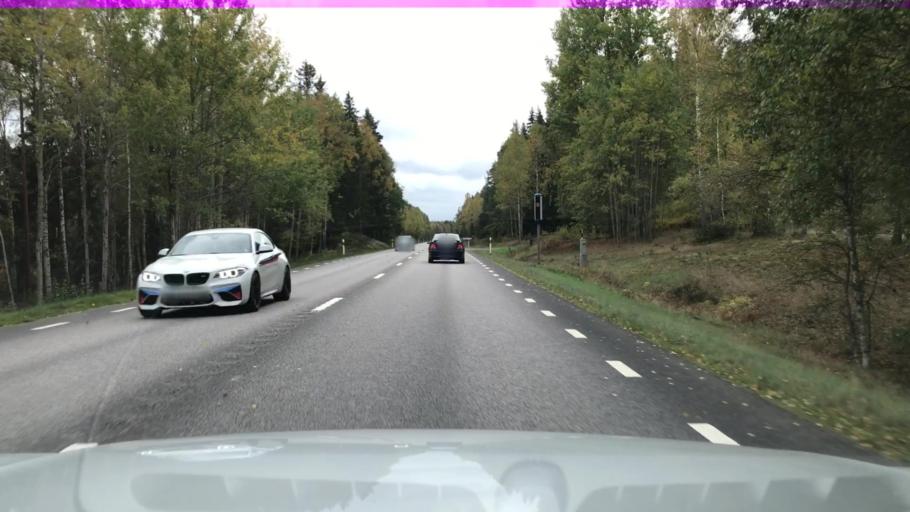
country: SE
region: Kalmar
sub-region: Hultsfreds Kommun
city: Hultsfred
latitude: 57.5492
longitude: 15.8454
